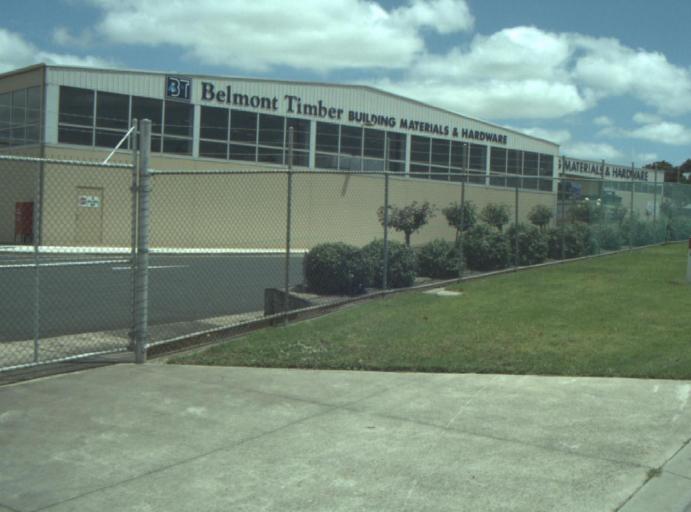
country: AU
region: Victoria
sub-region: Greater Geelong
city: Breakwater
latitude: -38.1807
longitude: 144.3523
